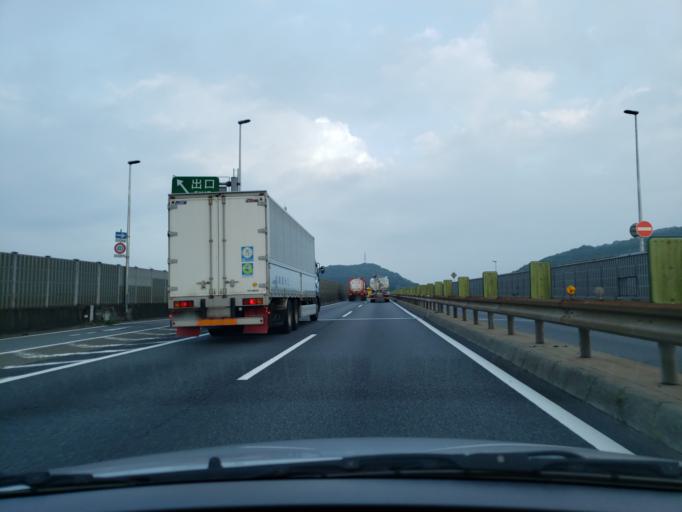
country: JP
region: Hyogo
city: Tatsunocho-tominaga
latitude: 34.8476
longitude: 134.5874
